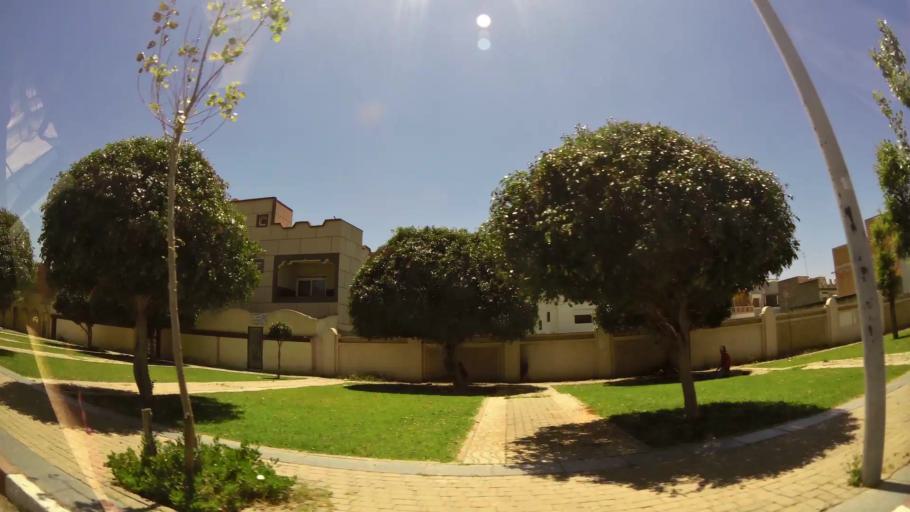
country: MA
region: Oriental
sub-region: Berkane-Taourirt
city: Madagh
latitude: 35.0829
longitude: -2.2206
